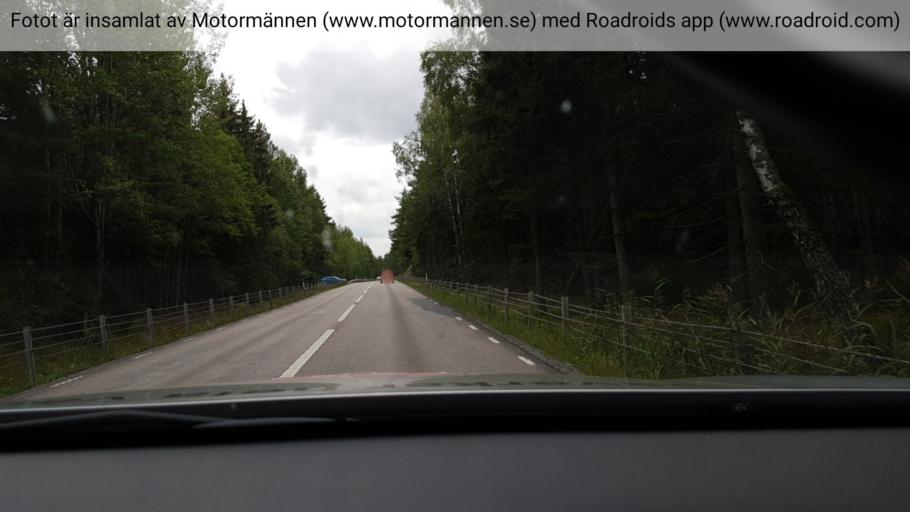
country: SE
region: Stockholm
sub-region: Sigtuna Kommun
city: Sigtuna
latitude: 59.6415
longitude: 17.7042
